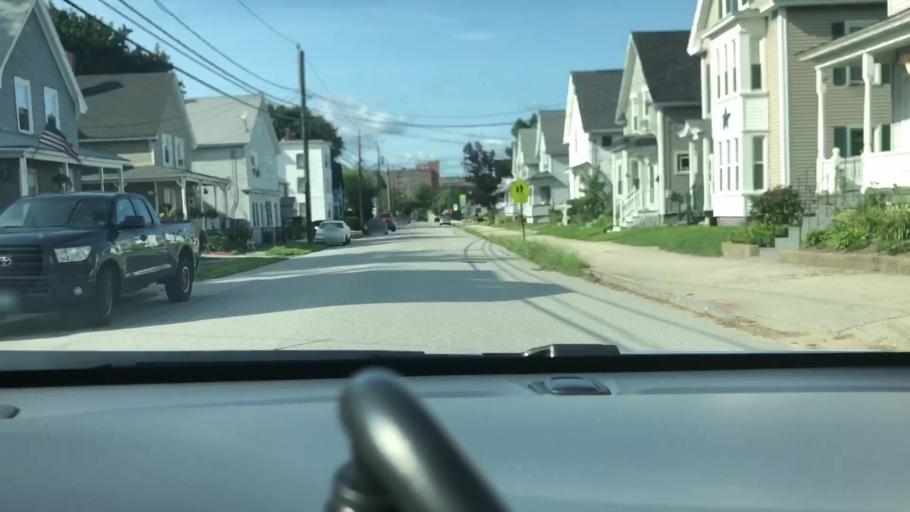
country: US
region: New Hampshire
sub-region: Hillsborough County
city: Manchester
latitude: 42.9785
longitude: -71.4381
